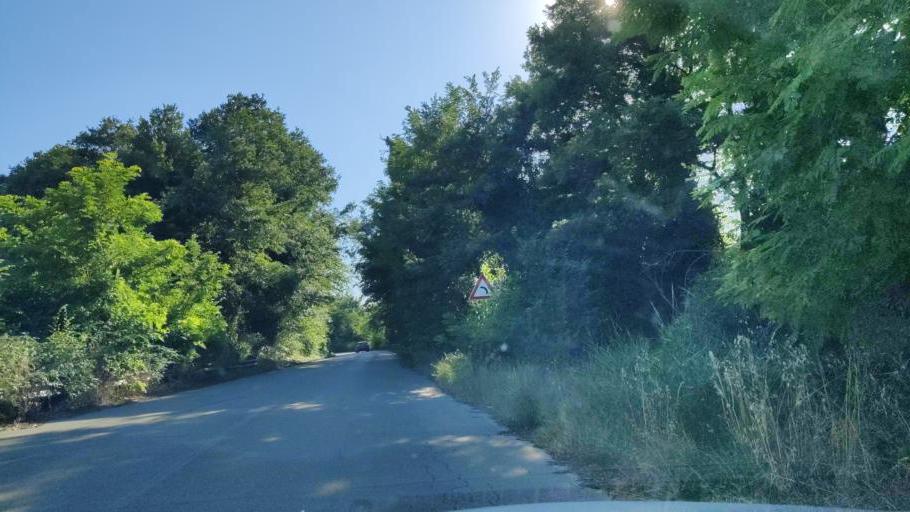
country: IT
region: Umbria
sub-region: Provincia di Terni
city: Penna in Teverina
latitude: 42.4762
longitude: 12.3665
